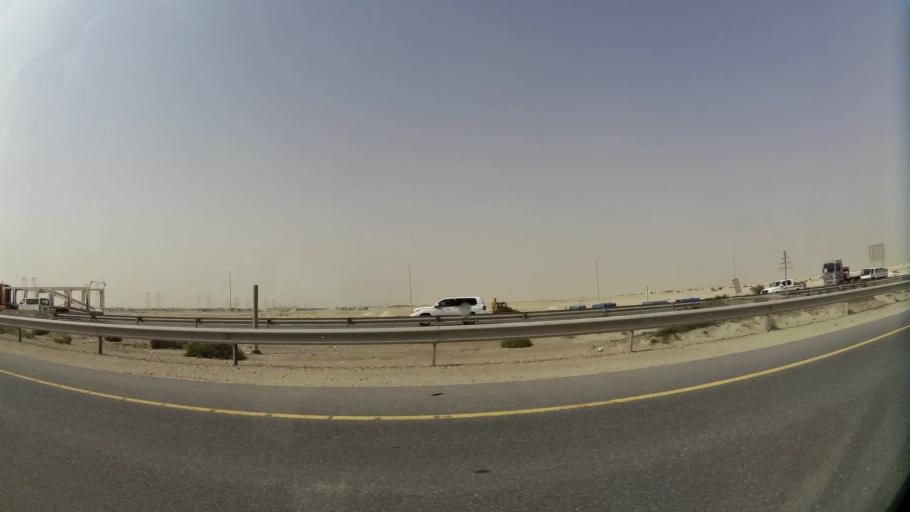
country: QA
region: Baladiyat ar Rayyan
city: Ar Rayyan
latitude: 25.1781
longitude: 51.3425
